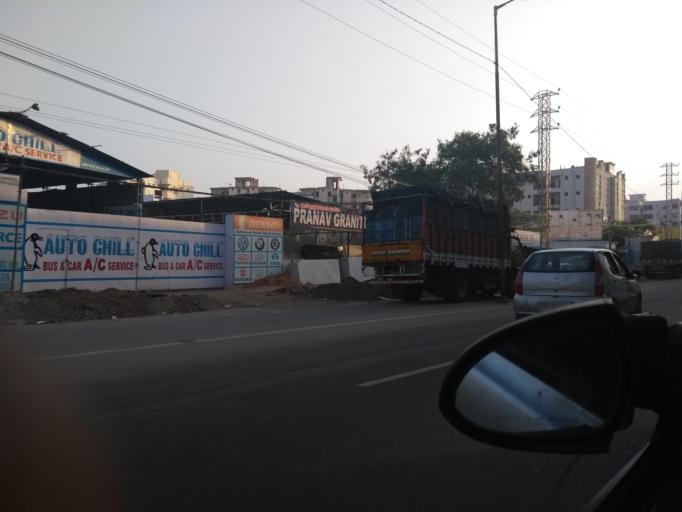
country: IN
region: Telangana
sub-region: Hyderabad
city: Hyderabad
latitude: 17.3528
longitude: 78.4187
